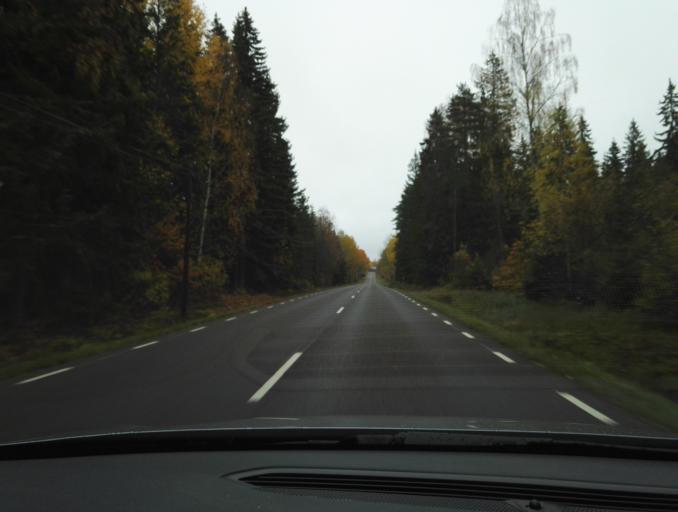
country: SE
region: Kronoberg
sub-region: Vaxjo Kommun
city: Rottne
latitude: 57.0253
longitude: 14.8619
